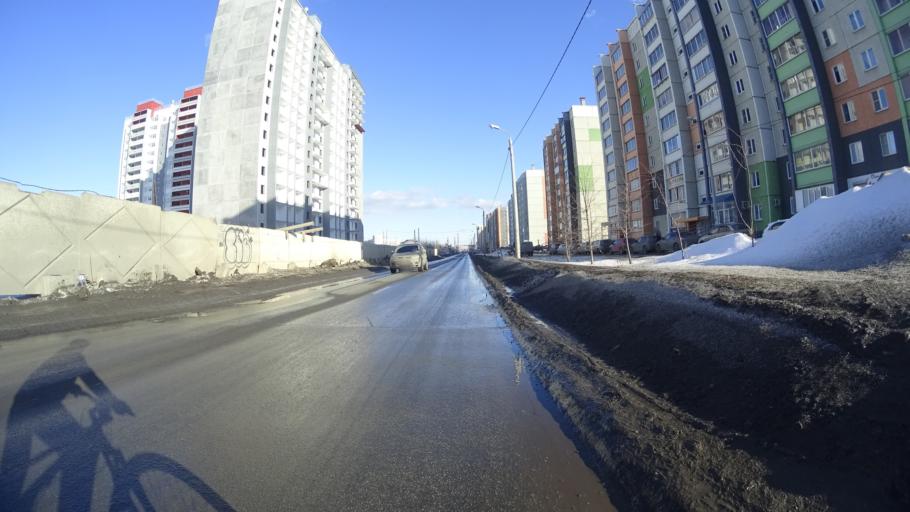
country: RU
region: Chelyabinsk
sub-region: Gorod Chelyabinsk
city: Chelyabinsk
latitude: 55.1671
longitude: 61.2873
